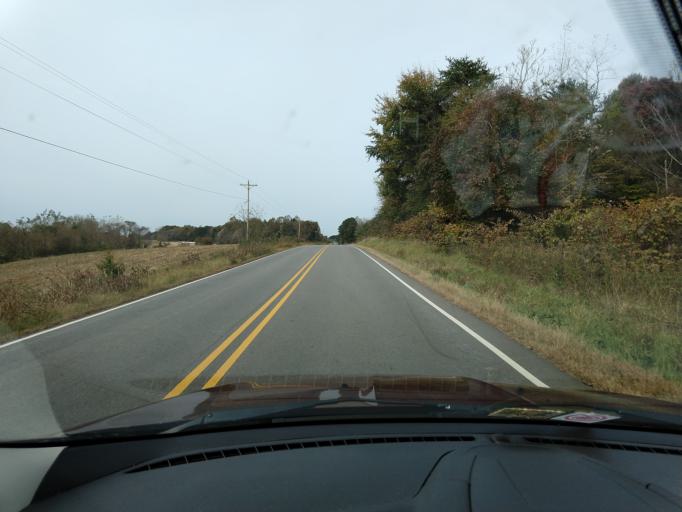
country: US
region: Virginia
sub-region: Franklin County
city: Union Hall
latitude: 36.9591
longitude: -79.5695
